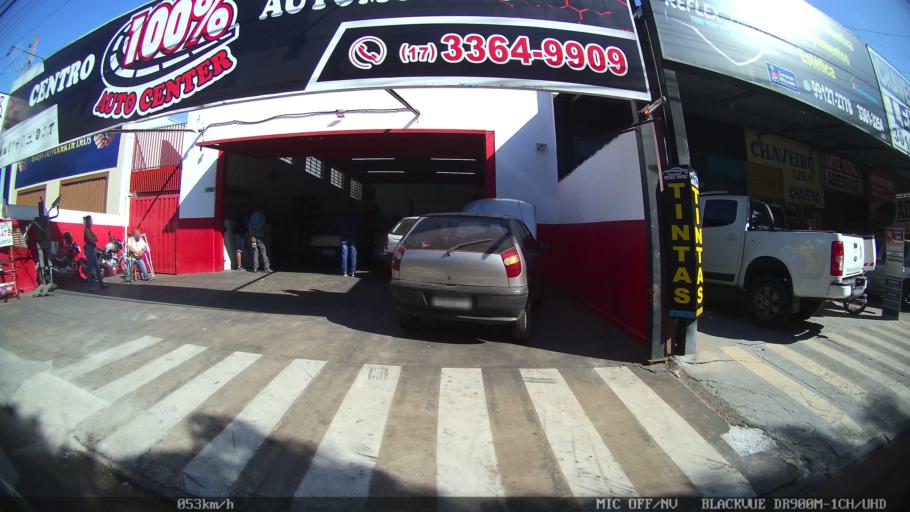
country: BR
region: Sao Paulo
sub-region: Sao Jose Do Rio Preto
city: Sao Jose do Rio Preto
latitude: -20.7730
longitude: -49.3855
